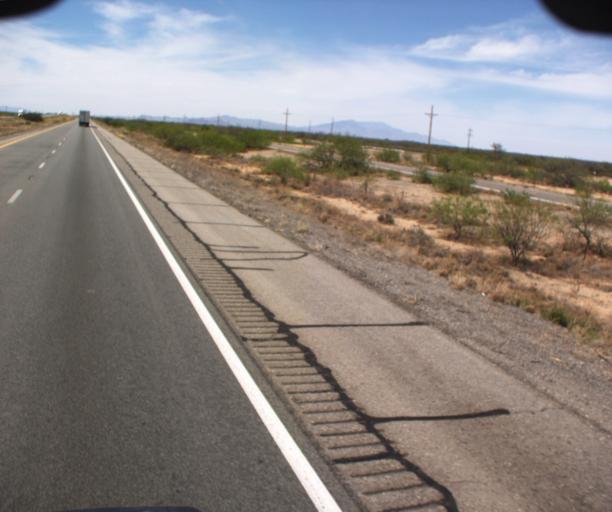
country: US
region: Arizona
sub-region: Cochise County
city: Willcox
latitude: 32.2949
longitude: -109.3427
